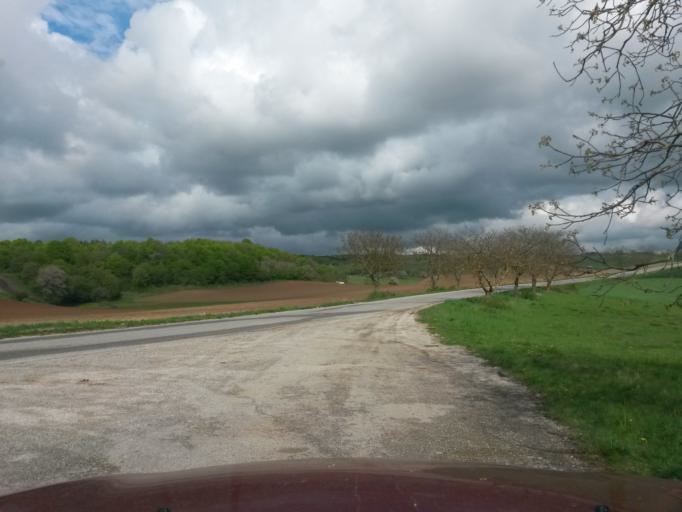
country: SK
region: Kosicky
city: Roznava
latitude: 48.5572
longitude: 20.5056
